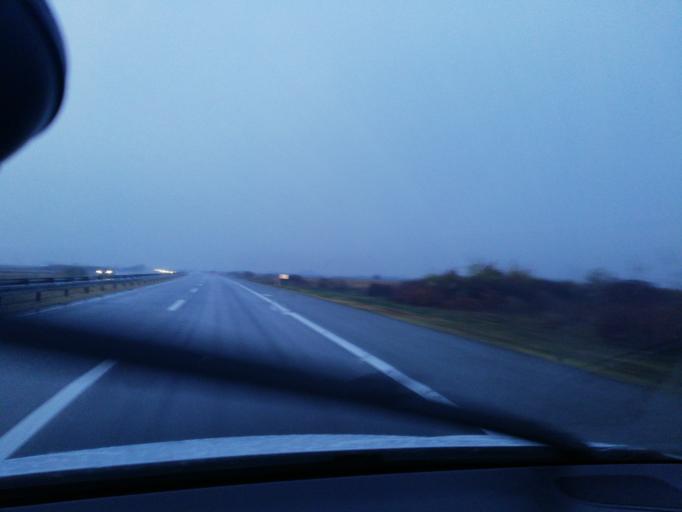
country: RS
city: Sasinci
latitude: 44.9945
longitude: 19.6985
